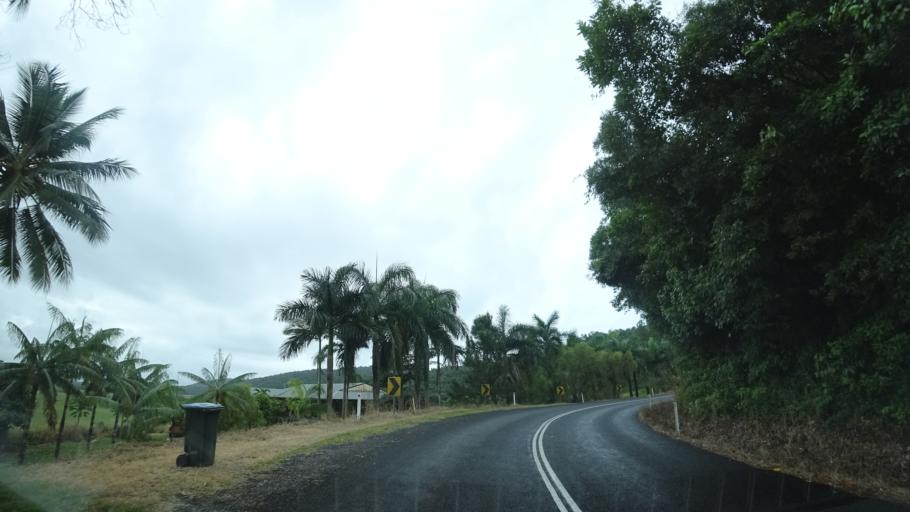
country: AU
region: Queensland
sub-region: Cassowary Coast
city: Innisfail
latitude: -17.5653
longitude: 146.0861
